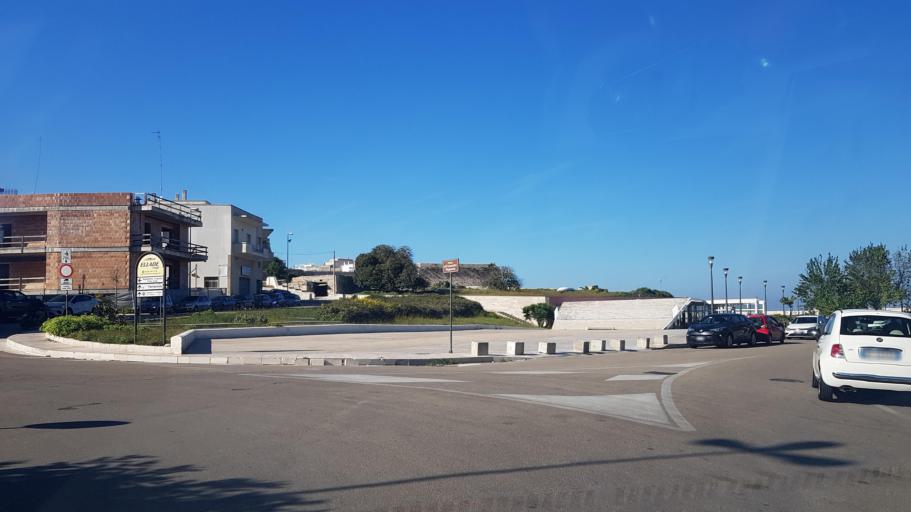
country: IT
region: Apulia
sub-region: Provincia di Lecce
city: Otranto
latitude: 40.1436
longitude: 18.4945
